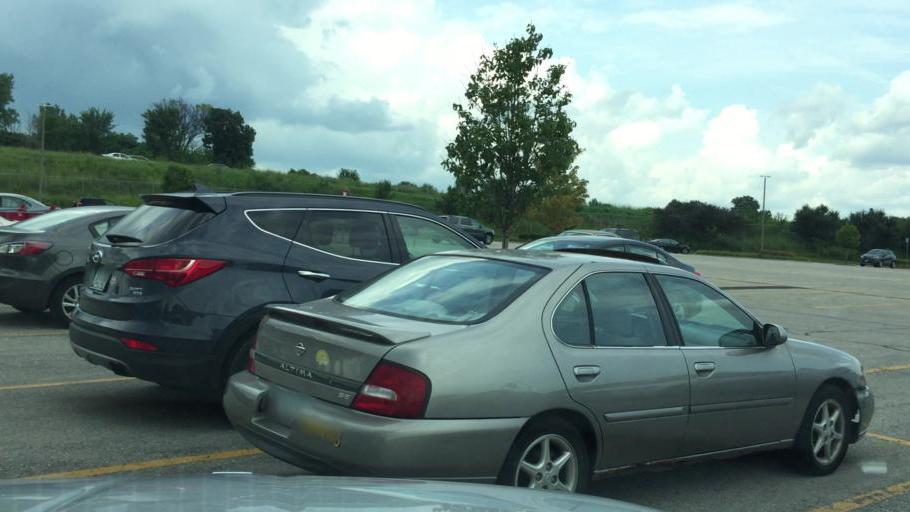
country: US
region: Iowa
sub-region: Johnson County
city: Coralville
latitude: 41.6923
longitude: -91.5994
